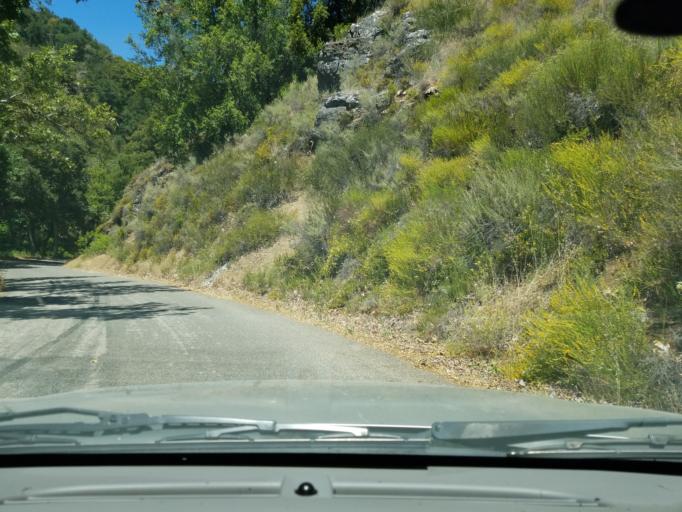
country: US
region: California
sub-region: Monterey County
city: Gonzales
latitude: 36.3588
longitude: -121.5501
